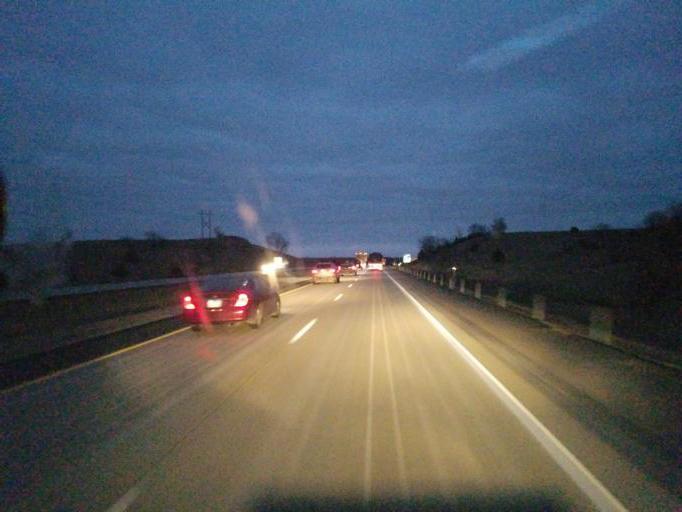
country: US
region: Iowa
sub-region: Cass County
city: Atlantic
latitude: 41.4968
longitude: -94.7684
